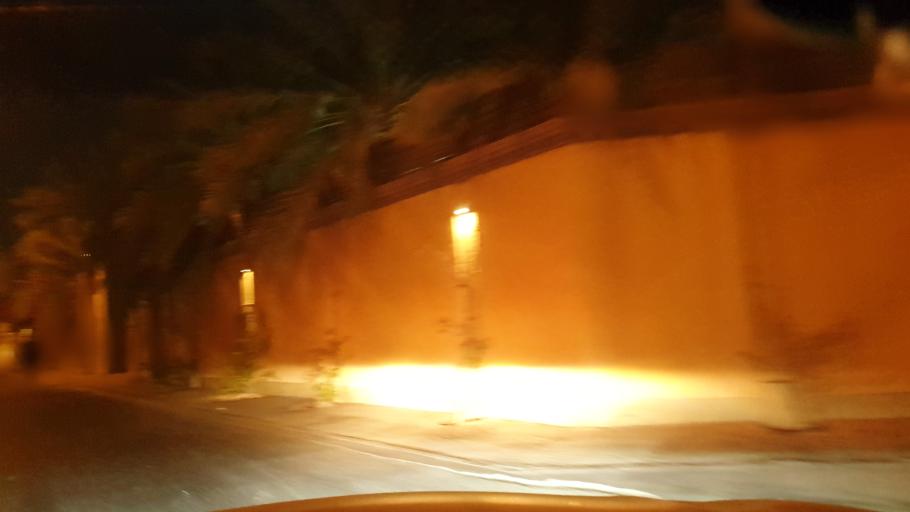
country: BH
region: Manama
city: Jidd Hafs
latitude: 26.1974
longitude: 50.4970
